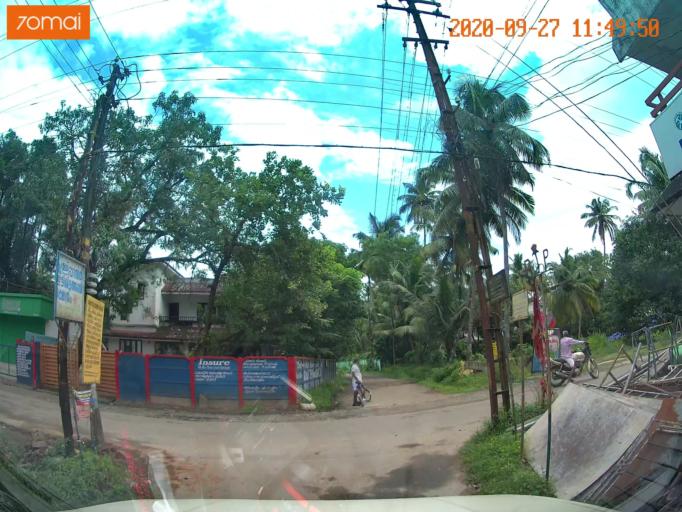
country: IN
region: Kerala
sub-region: Thrissur District
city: Thanniyam
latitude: 10.4715
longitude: 76.1158
